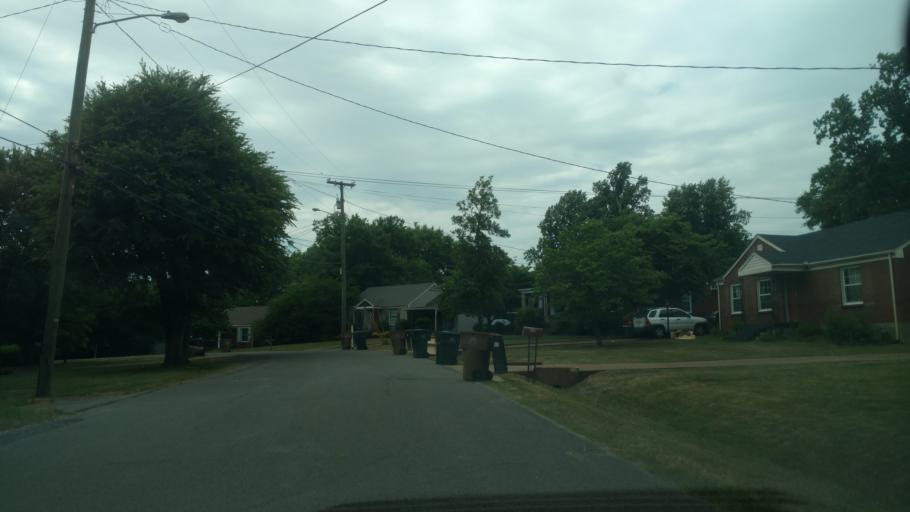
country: US
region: Tennessee
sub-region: Davidson County
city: Lakewood
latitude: 36.2100
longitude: -86.7080
